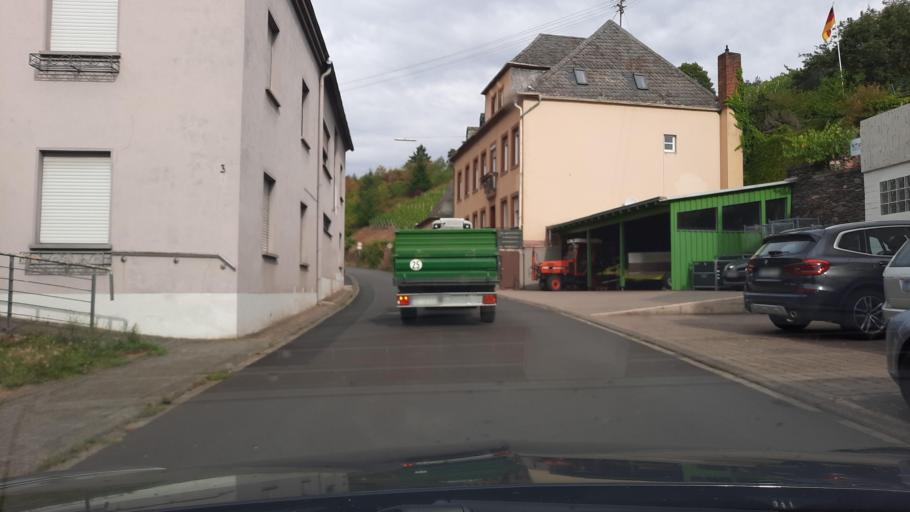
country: DE
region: Rheinland-Pfalz
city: Klusserath
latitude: 49.8440
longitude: 6.8438
